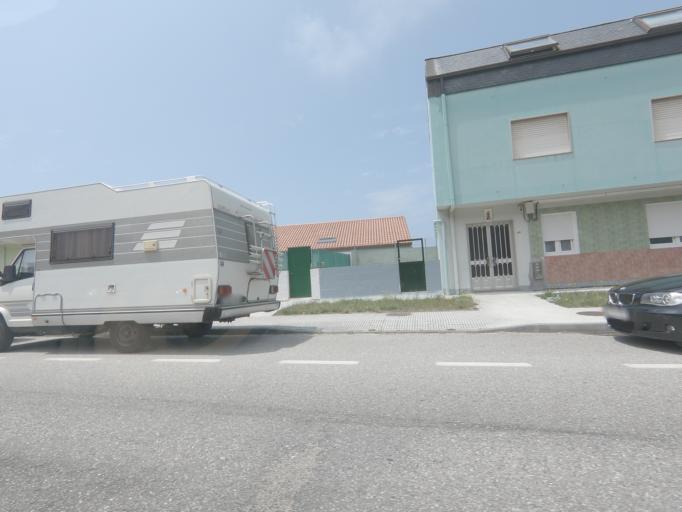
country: ES
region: Galicia
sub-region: Provincia de Pontevedra
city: A Guarda
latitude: 41.8953
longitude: -8.8755
